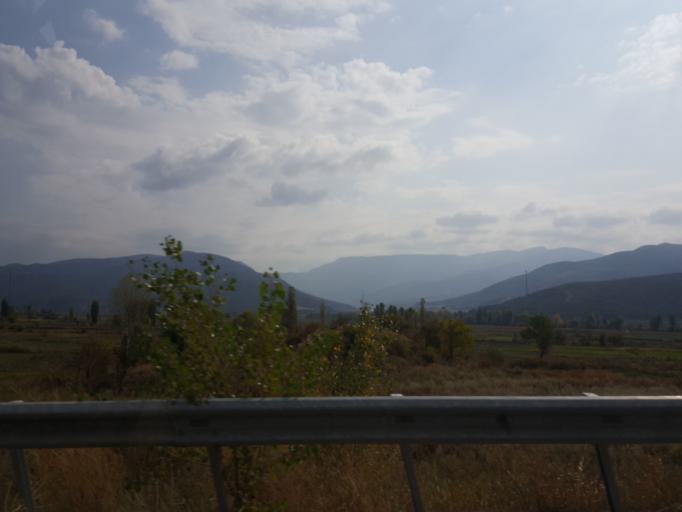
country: TR
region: Corum
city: Hacihamza
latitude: 41.1138
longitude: 34.3983
